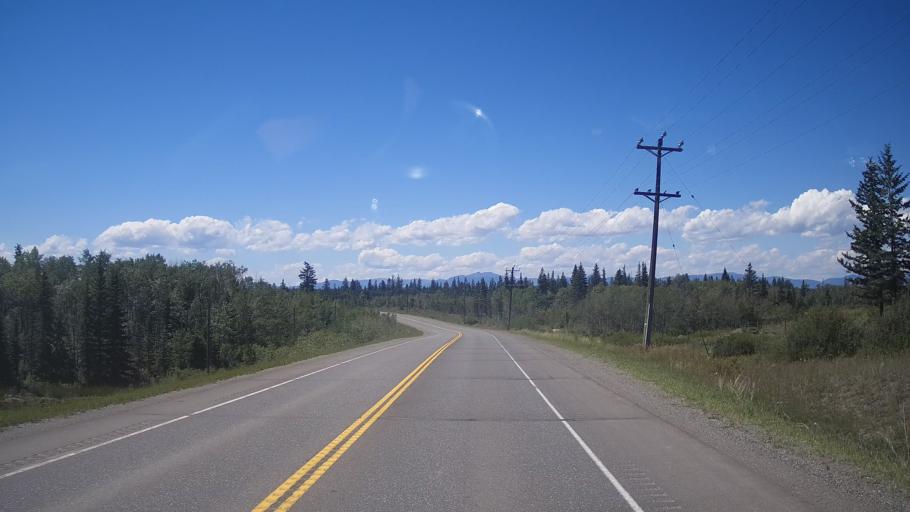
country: CA
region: British Columbia
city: Cache Creek
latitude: 51.2920
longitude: -121.4194
